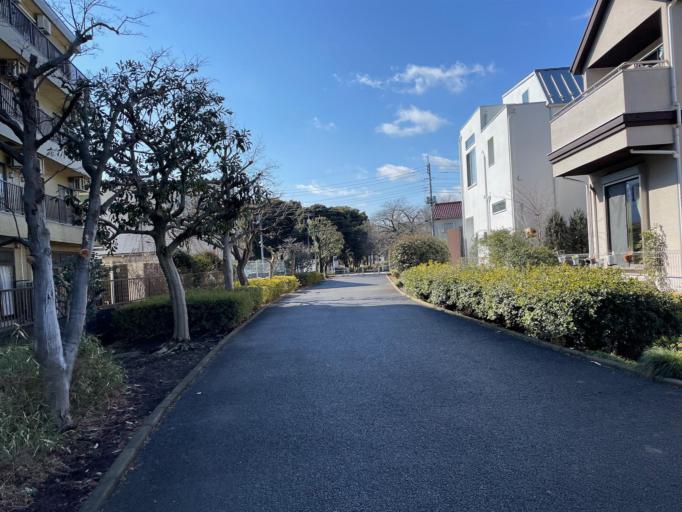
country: JP
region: Tokyo
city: Kokubunji
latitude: 35.6580
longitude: 139.4754
